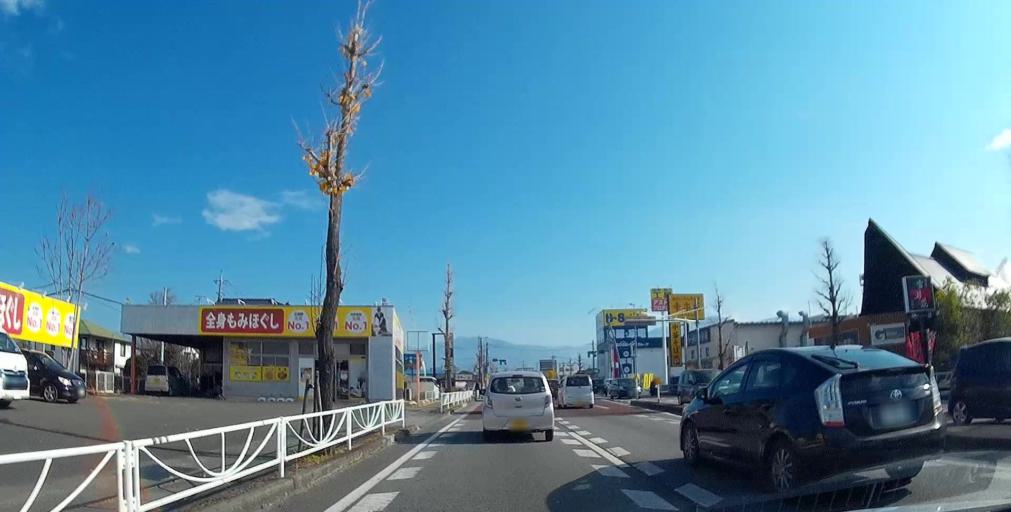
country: JP
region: Yamanashi
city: Isawa
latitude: 35.6458
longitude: 138.6144
